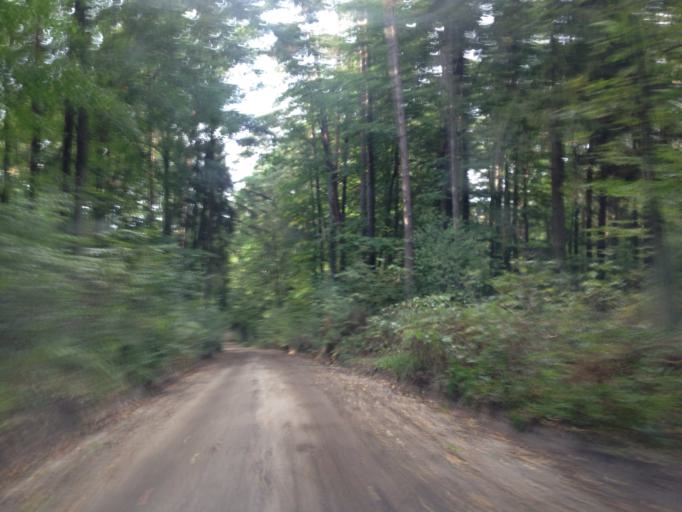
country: PL
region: Warmian-Masurian Voivodeship
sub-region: Powiat ilawski
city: Susz
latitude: 53.7595
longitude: 19.3037
